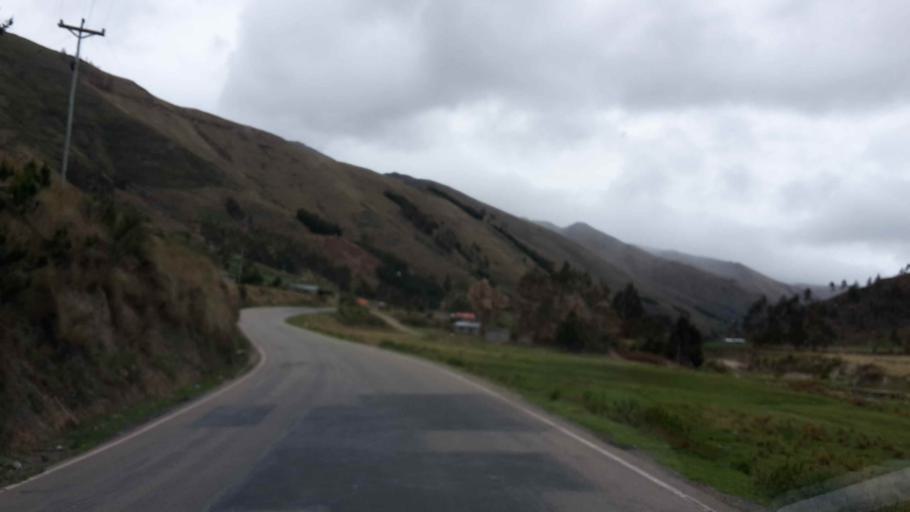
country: BO
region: Cochabamba
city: Arani
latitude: -17.4848
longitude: -65.5488
